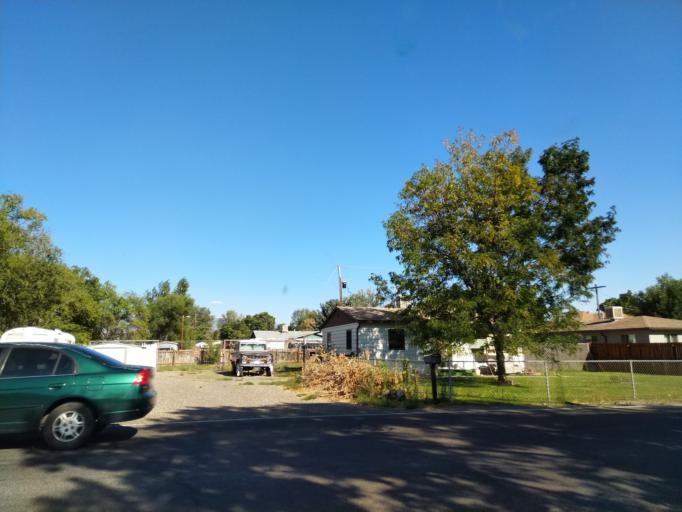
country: US
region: Colorado
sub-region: Mesa County
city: Orchard Mesa
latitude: 39.0429
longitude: -108.5247
